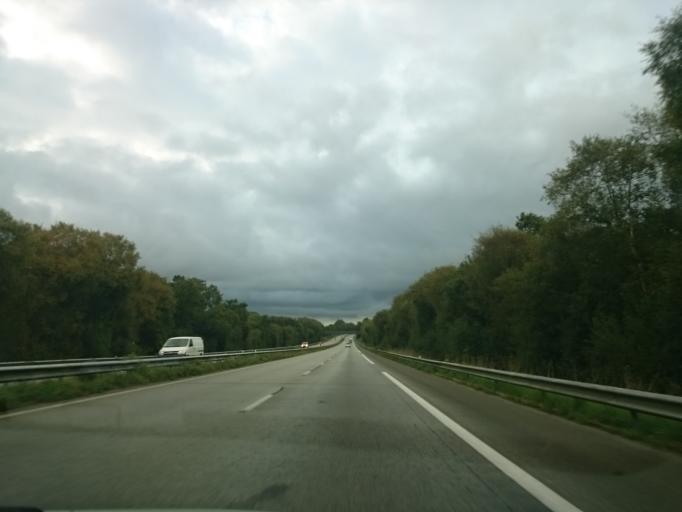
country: FR
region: Brittany
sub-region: Departement du Finistere
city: Briec
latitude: 48.1363
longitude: -4.0275
